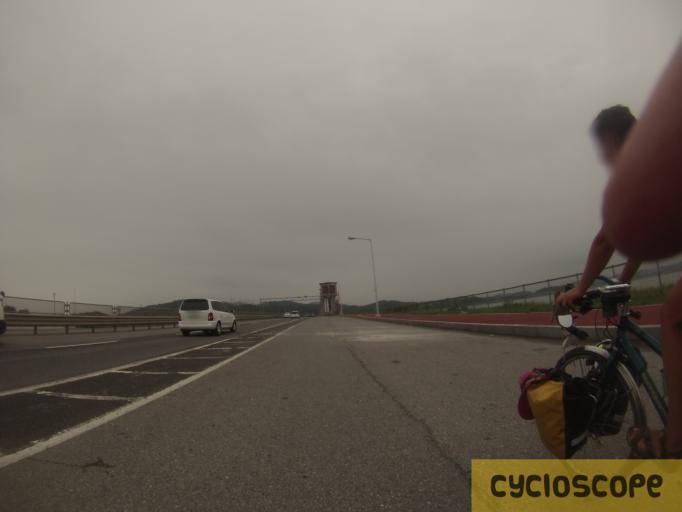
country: KR
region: Chungcheongnam-do
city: Taisen-ri
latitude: 36.1405
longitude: 126.5629
